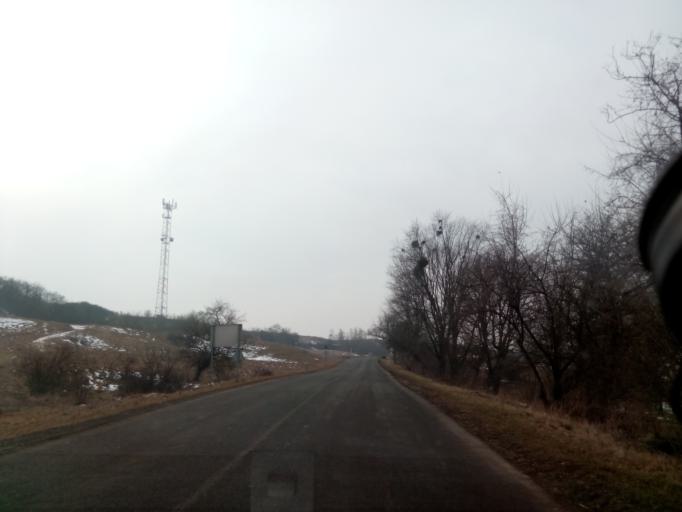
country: HU
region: Borsod-Abauj-Zemplen
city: Gonc
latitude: 48.4803
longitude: 21.2575
